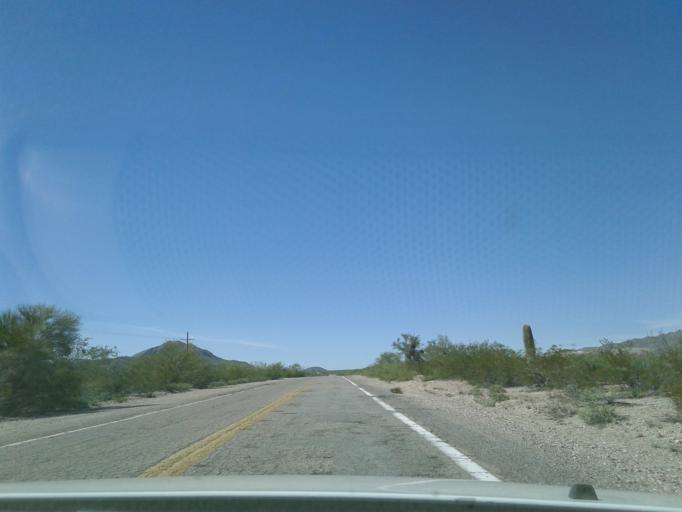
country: US
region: Arizona
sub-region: Pima County
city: Avra Valley
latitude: 32.3719
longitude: -111.4402
